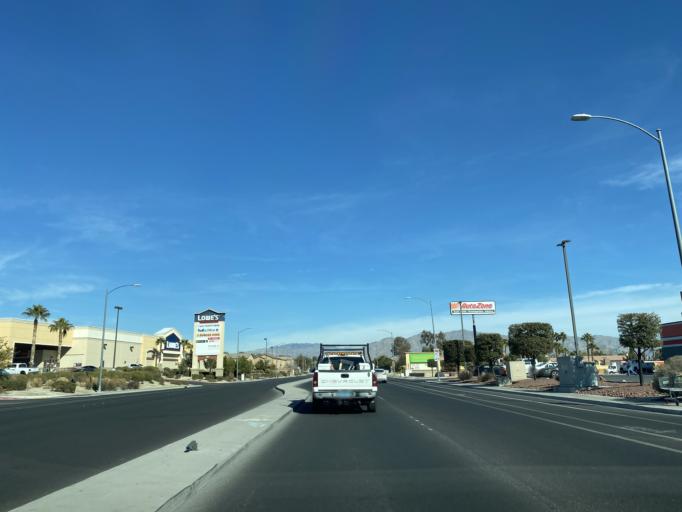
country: US
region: Nevada
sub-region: Clark County
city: Las Vegas
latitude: 36.2396
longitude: -115.2255
